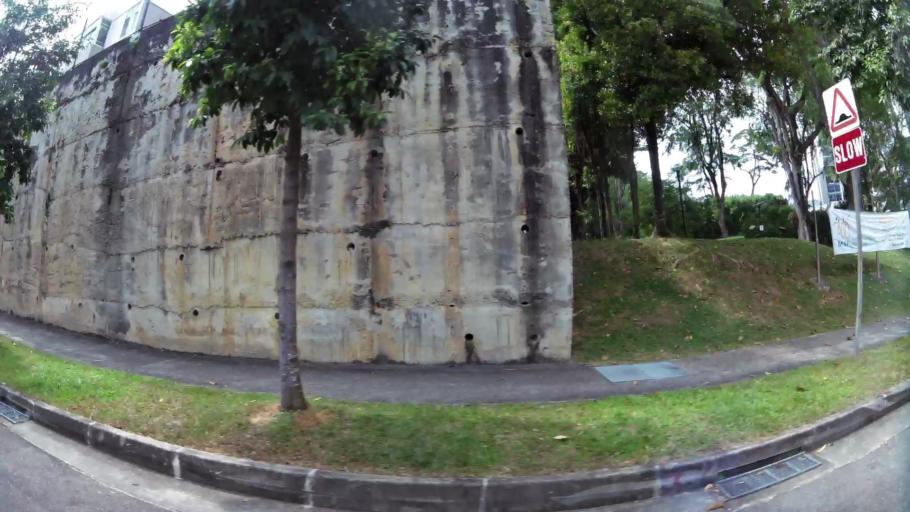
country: MY
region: Johor
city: Johor Bahru
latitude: 1.3757
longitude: 103.7576
